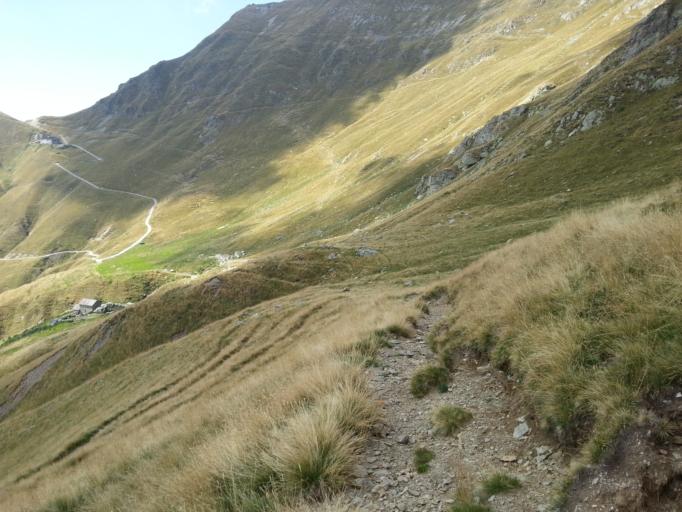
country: CH
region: Grisons
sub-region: Moesa District
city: Roveredo
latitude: 46.1659
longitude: 9.1707
